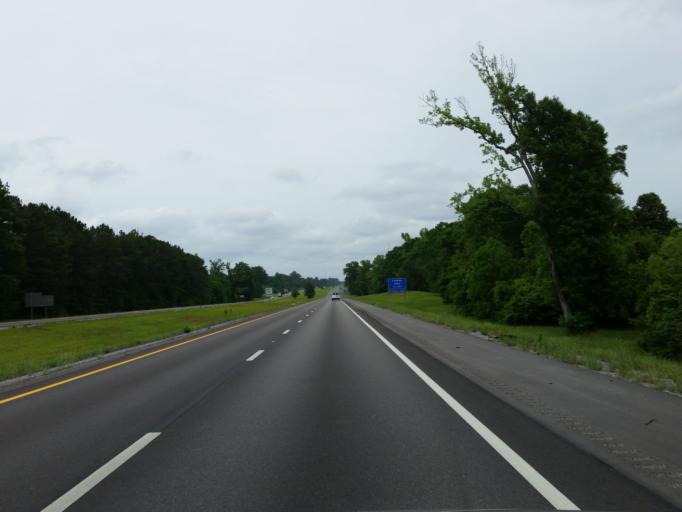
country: US
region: Mississippi
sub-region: Jones County
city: Sharon
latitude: 31.7938
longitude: -89.0543
